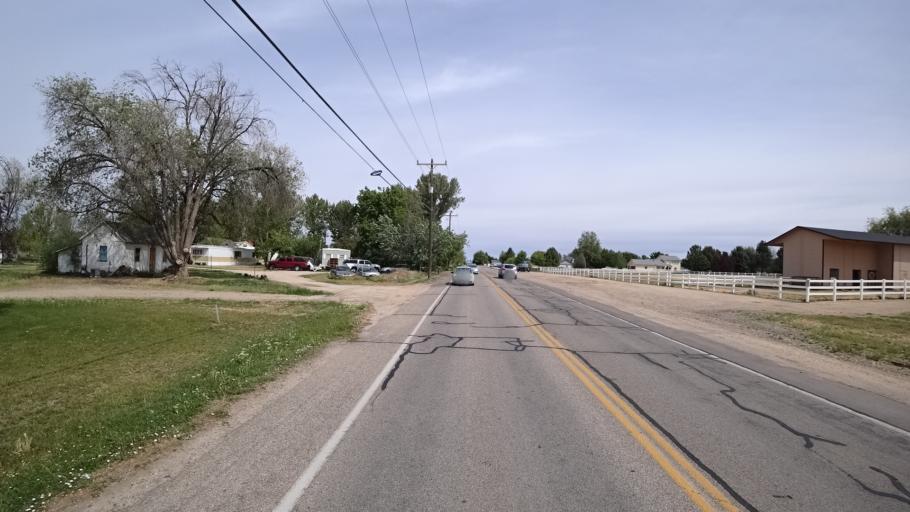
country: US
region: Idaho
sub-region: Ada County
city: Meridian
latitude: 43.5574
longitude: -116.3143
